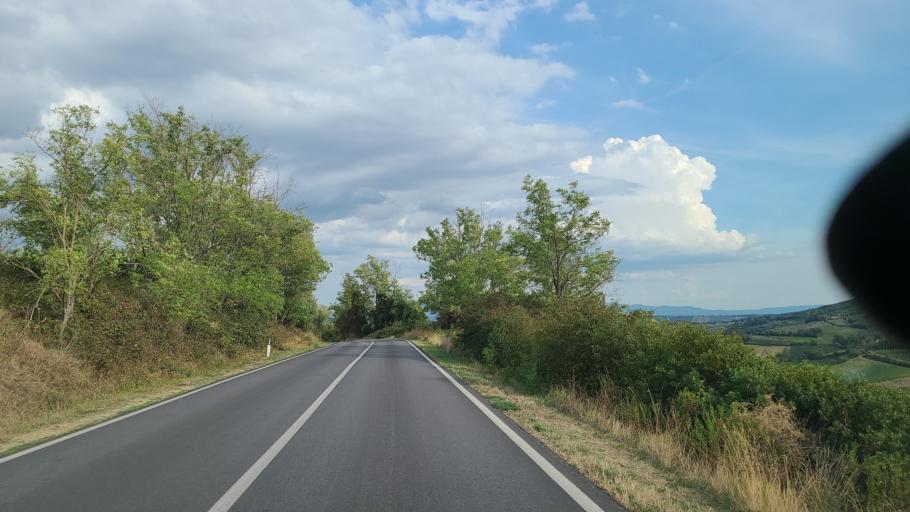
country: IT
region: Tuscany
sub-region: Provincia di Siena
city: San Gimignano
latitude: 43.4820
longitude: 11.0086
